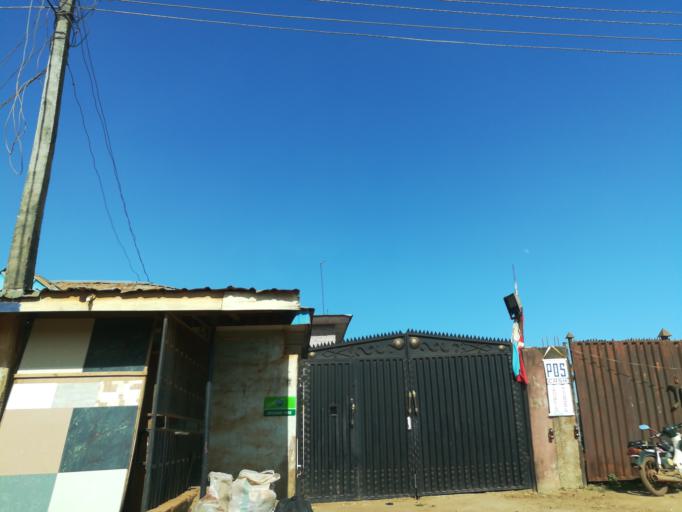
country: NG
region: Lagos
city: Ikorodu
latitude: 6.5817
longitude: 3.5228
